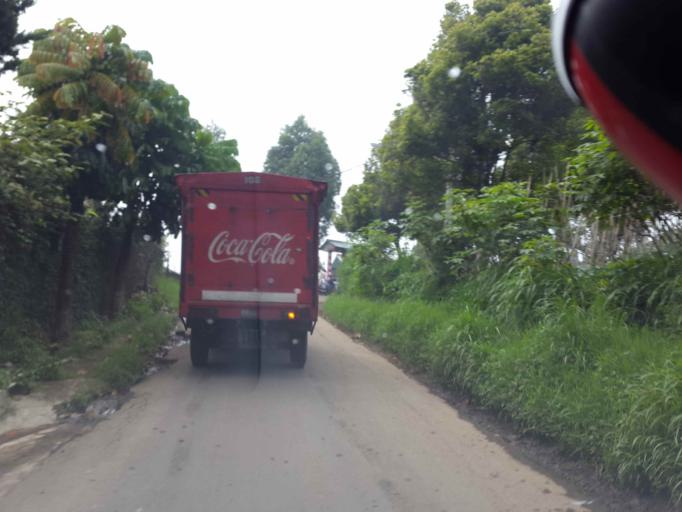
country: ID
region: West Java
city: Lembang
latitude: -6.8266
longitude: 107.5741
